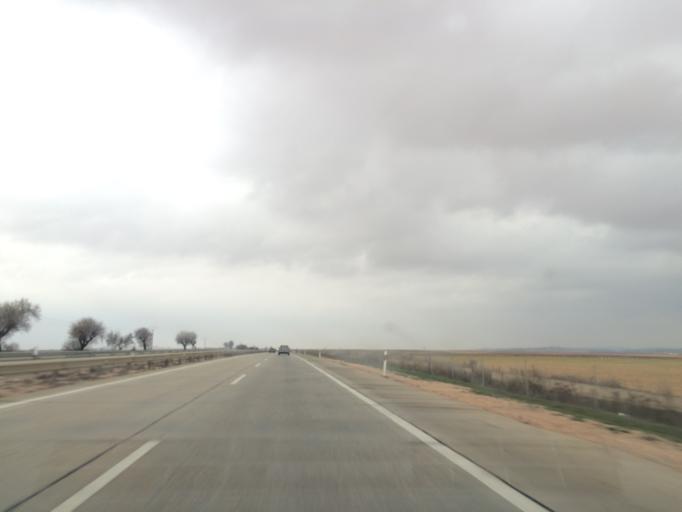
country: ES
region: Castille-La Mancha
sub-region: Province of Toledo
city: Madridejos
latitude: 39.5447
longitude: -3.5185
